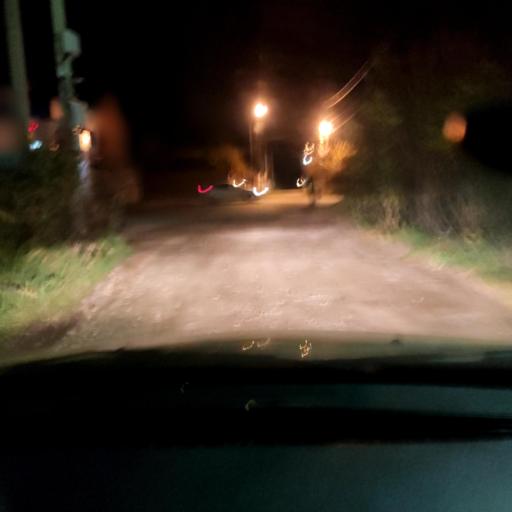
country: RU
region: Bashkortostan
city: Mikhaylovka
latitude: 54.8020
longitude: 55.9411
